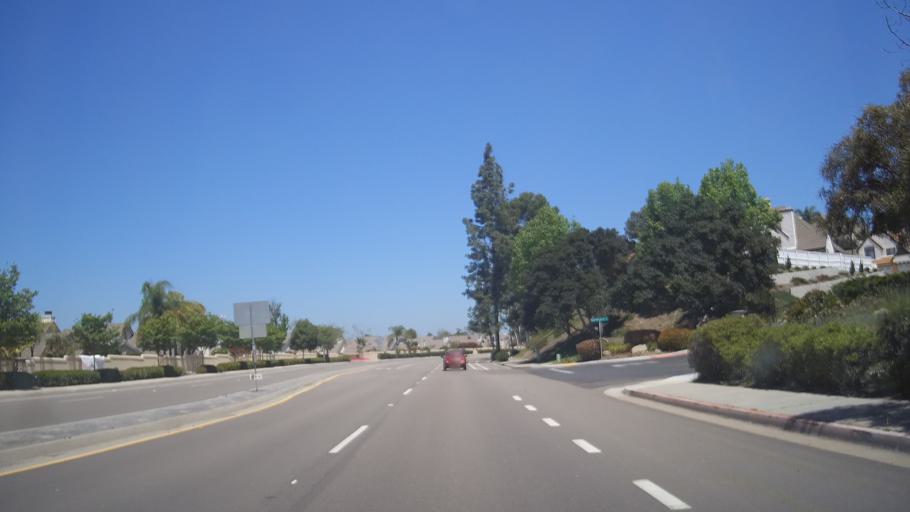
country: US
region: California
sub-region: San Diego County
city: Poway
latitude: 32.9677
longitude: -117.0895
